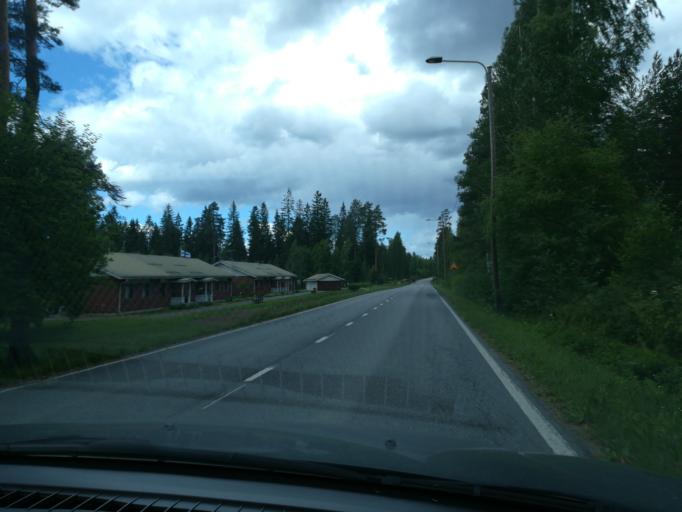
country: FI
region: Southern Savonia
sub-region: Mikkeli
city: Hirvensalmi
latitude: 61.6567
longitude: 26.7666
